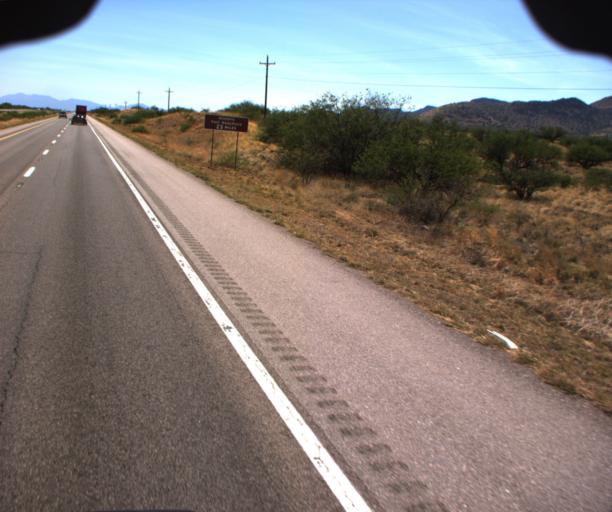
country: US
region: Arizona
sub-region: Cochise County
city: Whetstone
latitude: 31.8752
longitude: -110.3413
